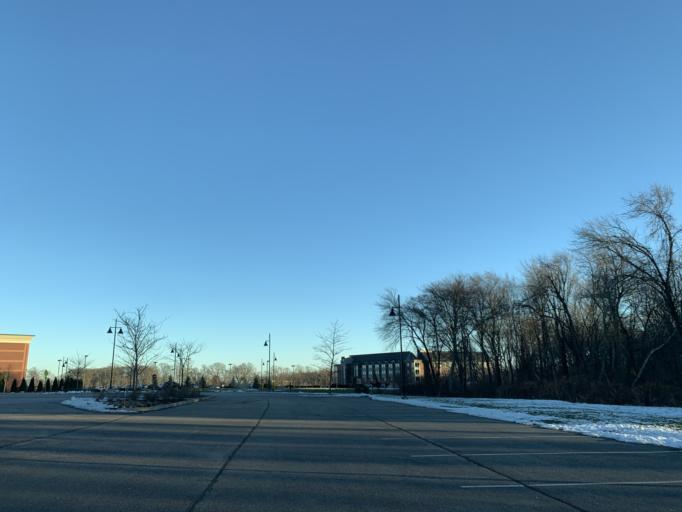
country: US
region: Rhode Island
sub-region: Kent County
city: West Warwick
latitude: 41.6615
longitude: -71.5057
